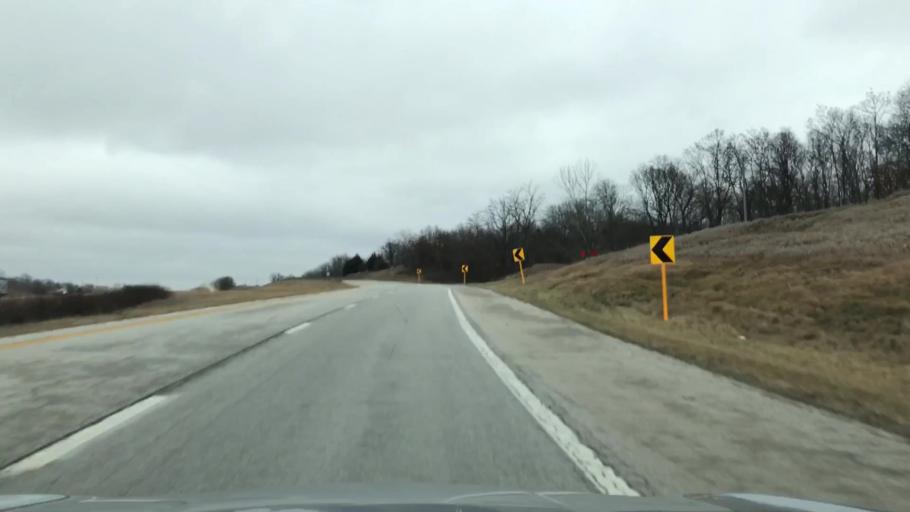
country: US
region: Missouri
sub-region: Linn County
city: Marceline
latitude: 39.7607
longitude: -92.9298
